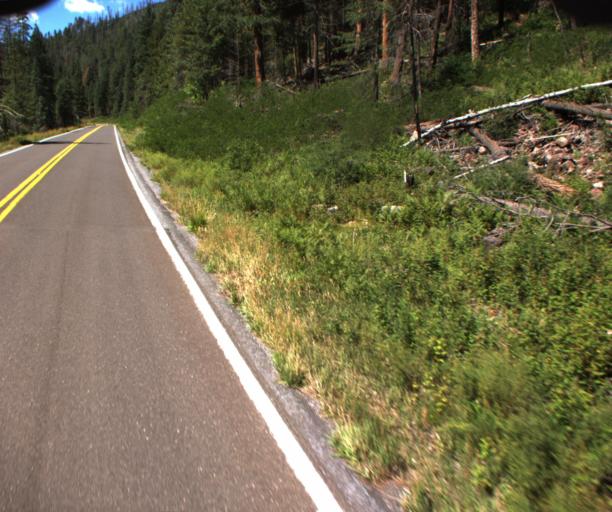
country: US
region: Arizona
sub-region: Apache County
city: Eagar
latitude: 33.6674
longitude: -109.2584
